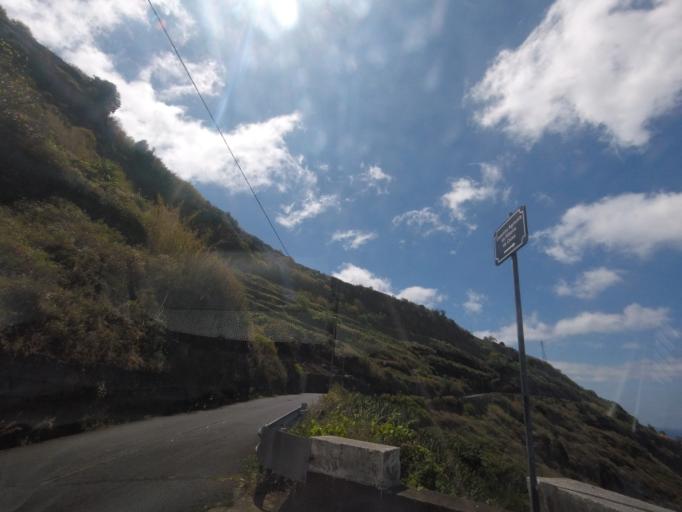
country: PT
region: Madeira
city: Ponta do Sol
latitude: 32.6868
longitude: -17.0828
